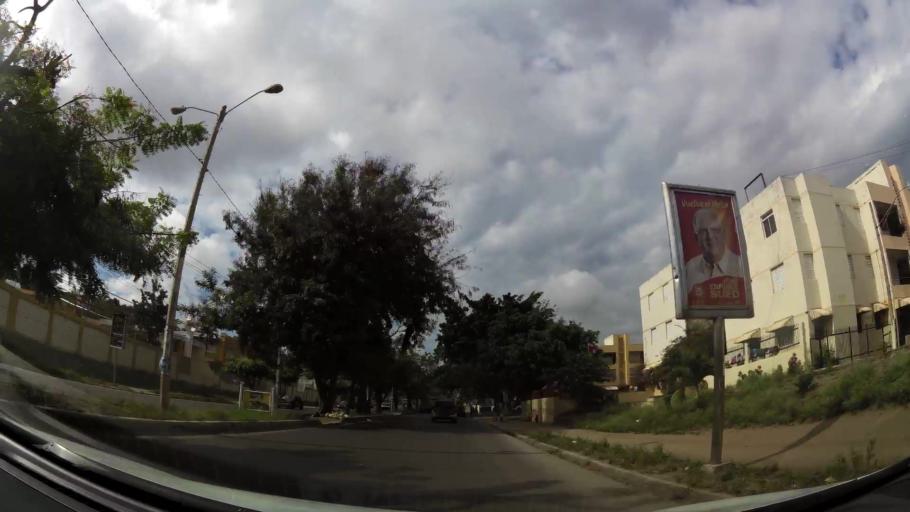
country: DO
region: Santiago
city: Santiago de los Caballeros
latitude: 19.4234
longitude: -70.6983
